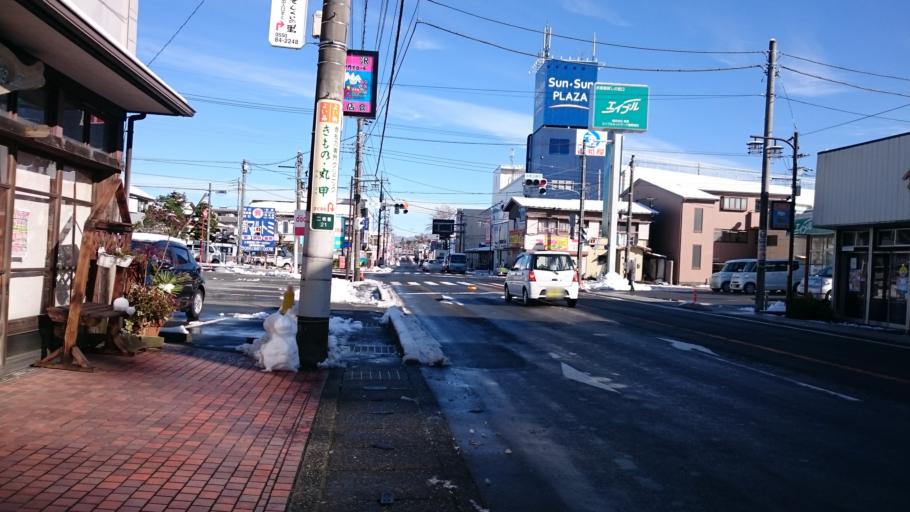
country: JP
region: Shizuoka
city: Gotemba
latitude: 35.3042
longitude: 138.9334
